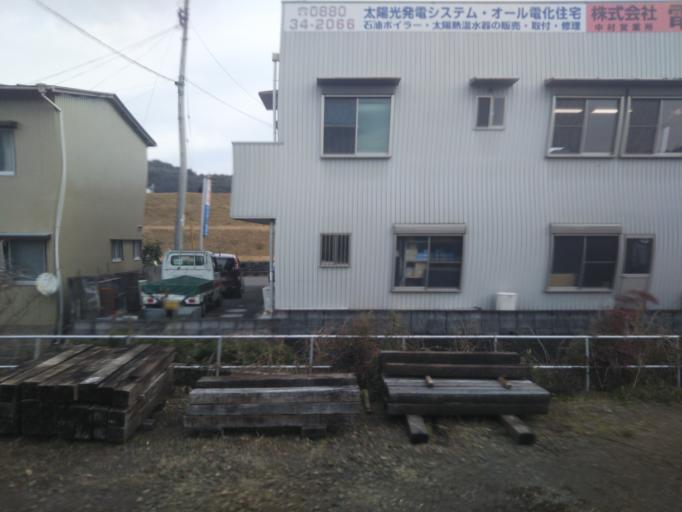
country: JP
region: Kochi
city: Nakamura
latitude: 32.9829
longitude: 132.9455
